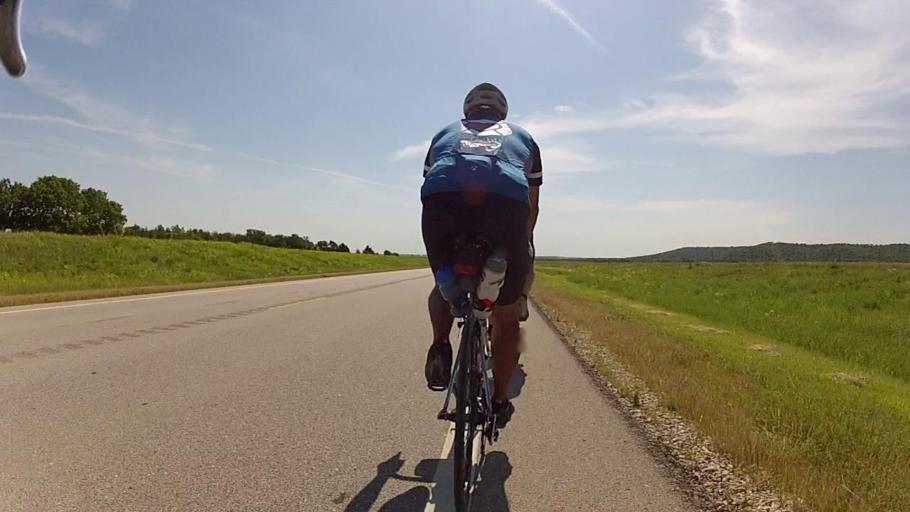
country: US
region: Kansas
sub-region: Chautauqua County
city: Sedan
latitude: 37.1069
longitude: -96.5646
